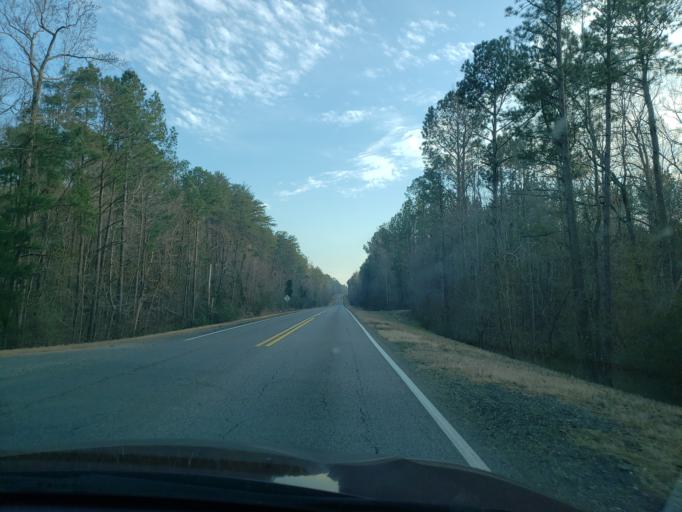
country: US
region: Alabama
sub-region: Hale County
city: Greensboro
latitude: 32.7546
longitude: -87.5852
